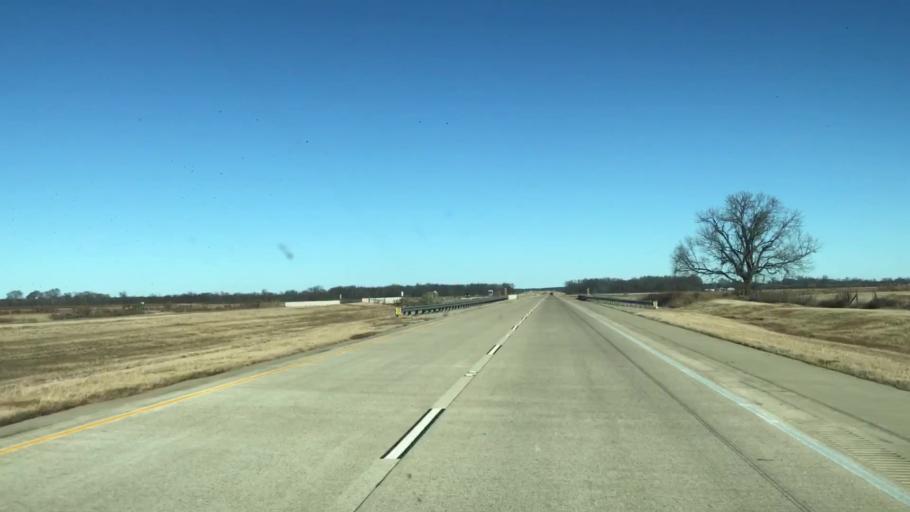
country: US
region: Louisiana
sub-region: Caddo Parish
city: Oil City
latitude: 32.7299
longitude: -93.8729
